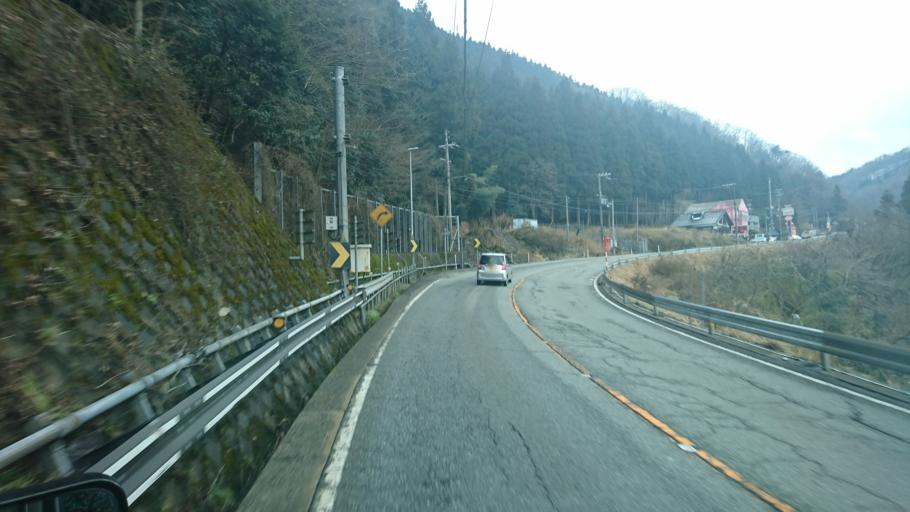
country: JP
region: Hyogo
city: Toyooka
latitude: 35.4887
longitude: 134.5750
